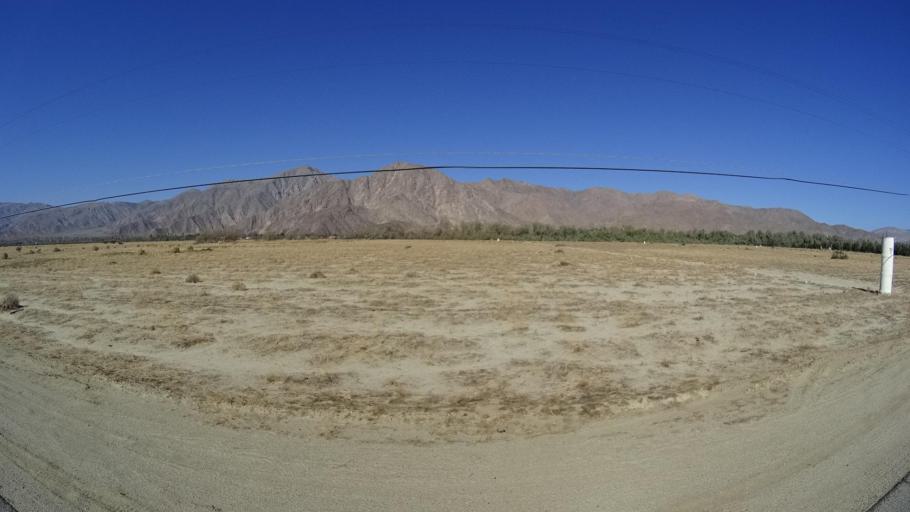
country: US
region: California
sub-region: San Diego County
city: Borrego Springs
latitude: 33.2986
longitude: -116.3667
